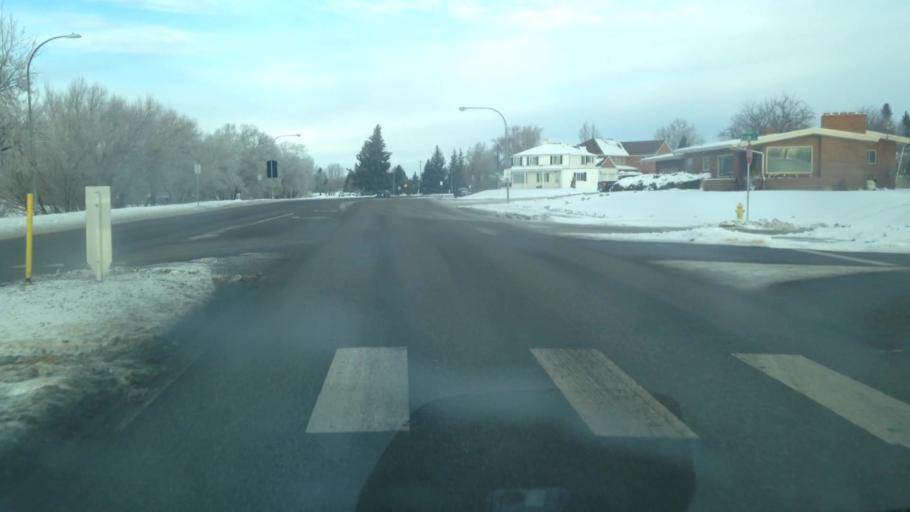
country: US
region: Idaho
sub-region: Bonneville County
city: Idaho Falls
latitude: 43.5037
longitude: -112.0452
